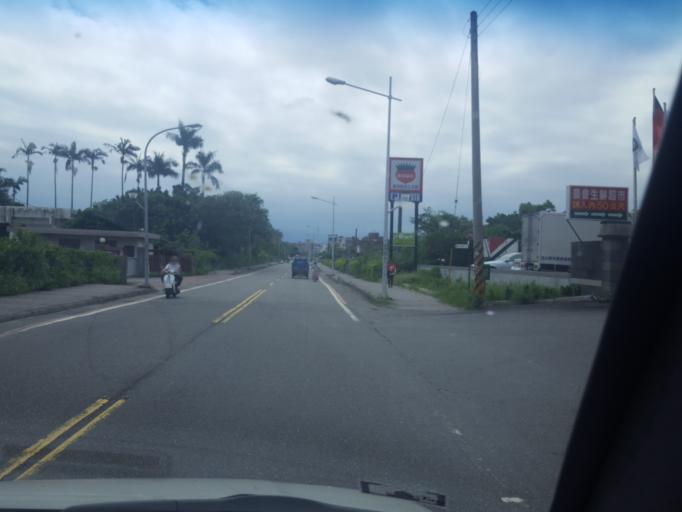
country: TW
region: Taiwan
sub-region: Yilan
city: Yilan
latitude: 24.7560
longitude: 121.7601
